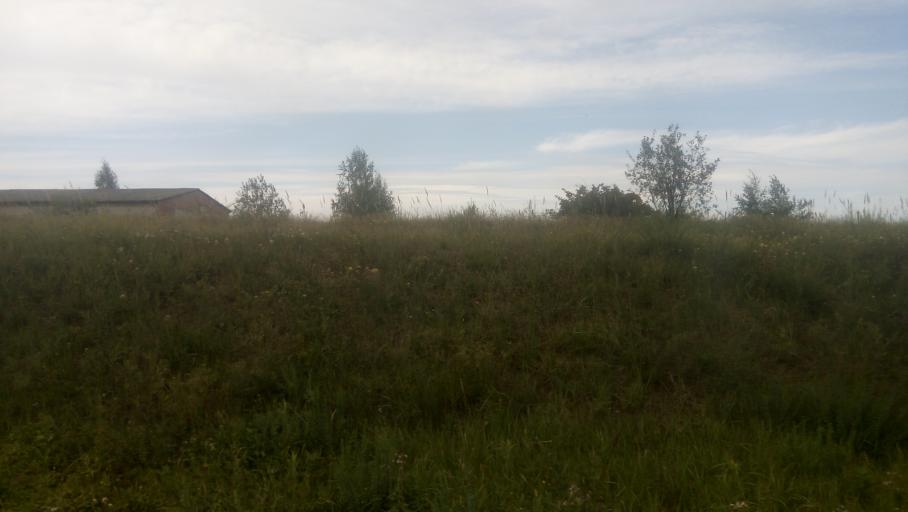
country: RU
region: Moskovskaya
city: Kabanovo
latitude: 55.7639
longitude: 38.9388
